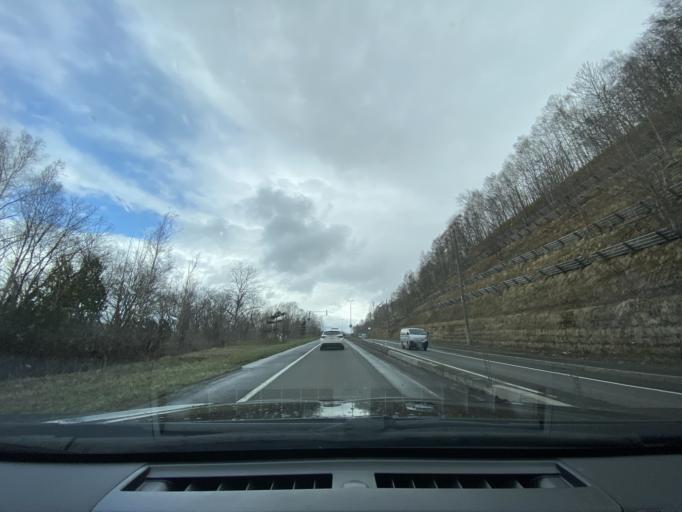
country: JP
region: Hokkaido
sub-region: Asahikawa-shi
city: Asahikawa
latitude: 43.7591
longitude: 142.2772
